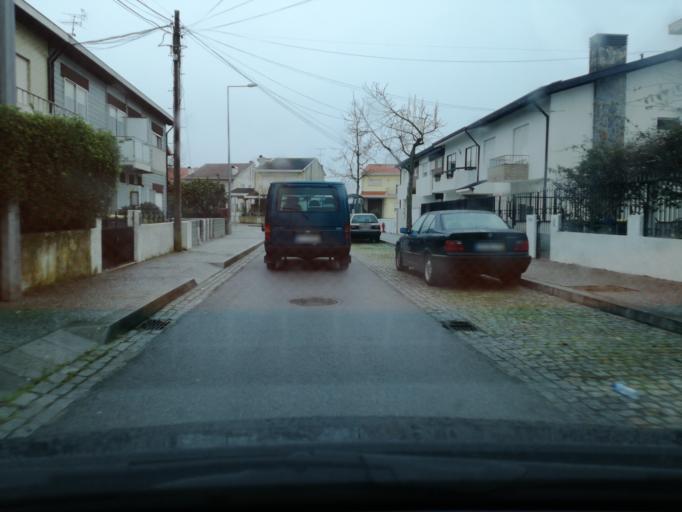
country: PT
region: Porto
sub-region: Maia
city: Gemunde
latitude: 41.2562
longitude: -8.6650
